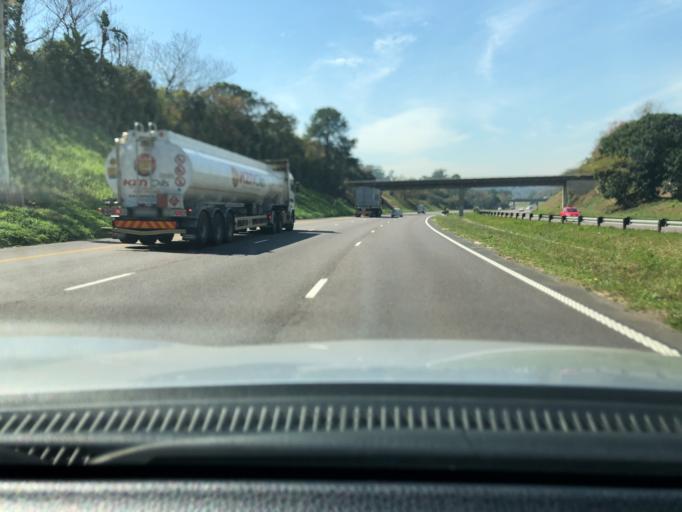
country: ZA
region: KwaZulu-Natal
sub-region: eThekwini Metropolitan Municipality
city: Berea
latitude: -29.8342
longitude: 30.8817
